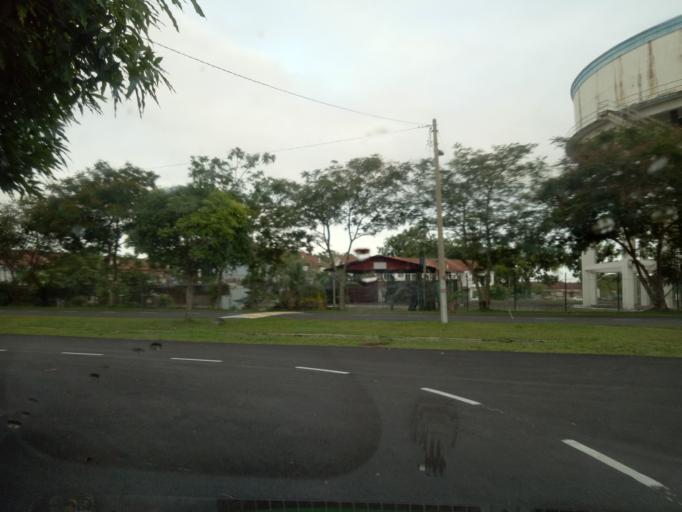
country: MY
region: Selangor
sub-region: Hulu Langat
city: Semenyih
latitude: 2.9322
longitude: 101.8627
